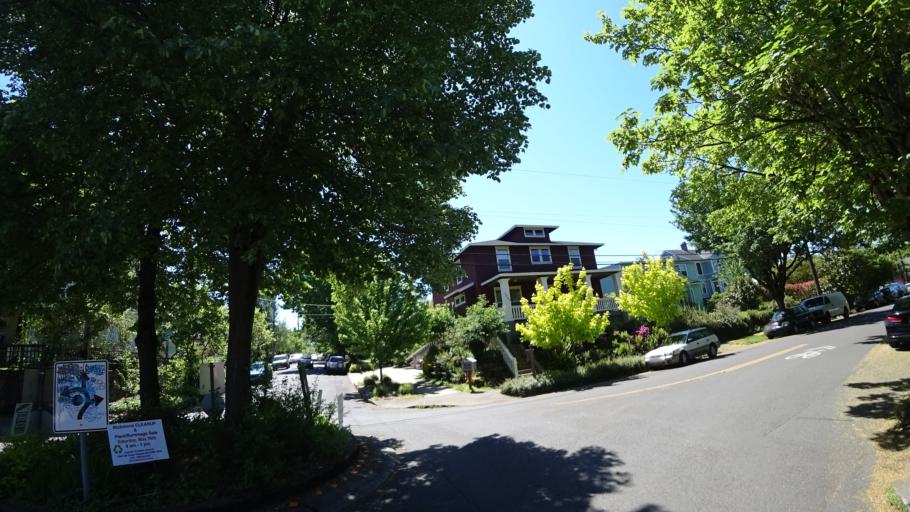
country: US
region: Oregon
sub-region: Multnomah County
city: Portland
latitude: 45.5035
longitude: -122.6263
